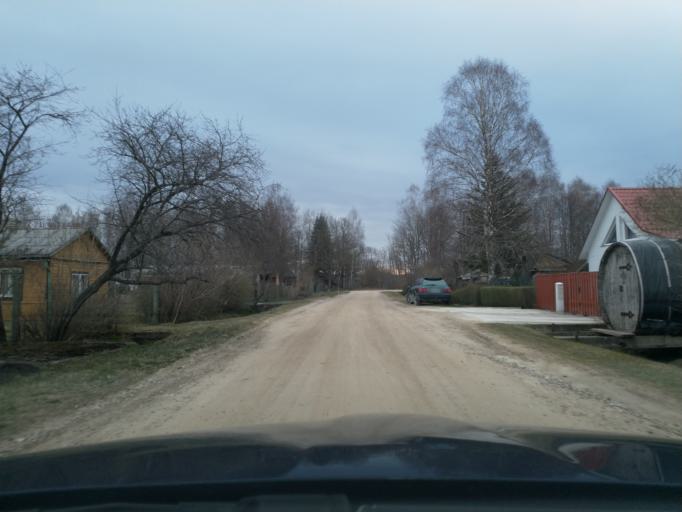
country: LV
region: Kuldigas Rajons
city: Kuldiga
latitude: 56.9536
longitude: 21.9987
